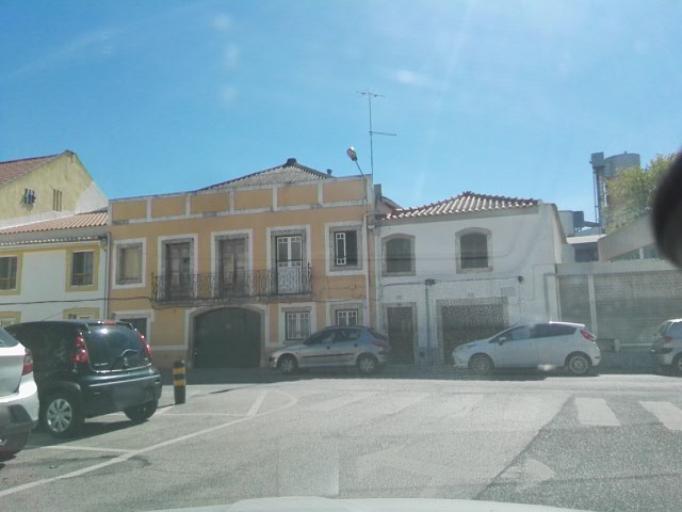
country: PT
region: Lisbon
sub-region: Vila Franca de Xira
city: Alhandra
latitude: 38.9248
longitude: -9.0106
